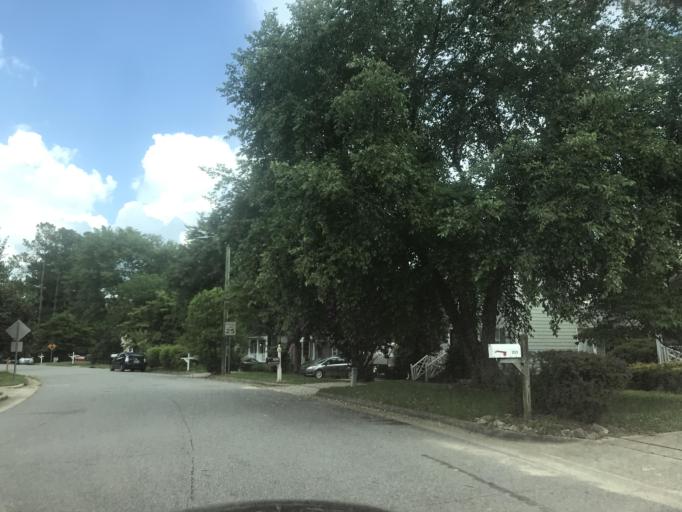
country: US
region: North Carolina
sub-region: Wake County
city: Raleigh
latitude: 35.8328
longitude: -78.5668
